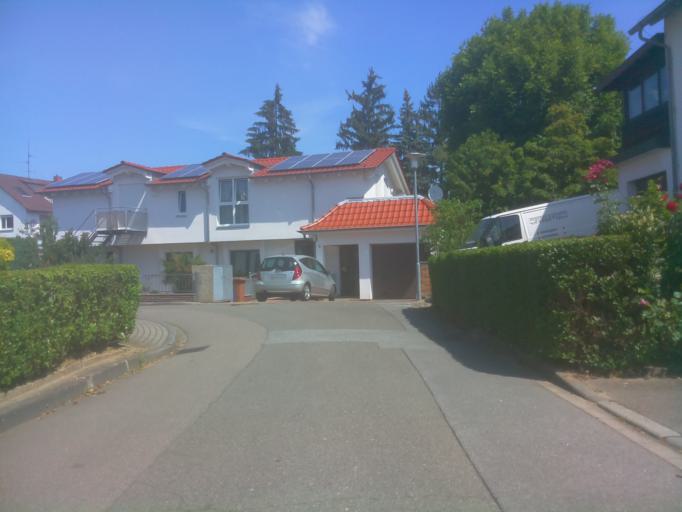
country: DE
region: Baden-Wuerttemberg
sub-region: Karlsruhe Region
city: Hemsbach
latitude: 49.5915
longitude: 8.6410
